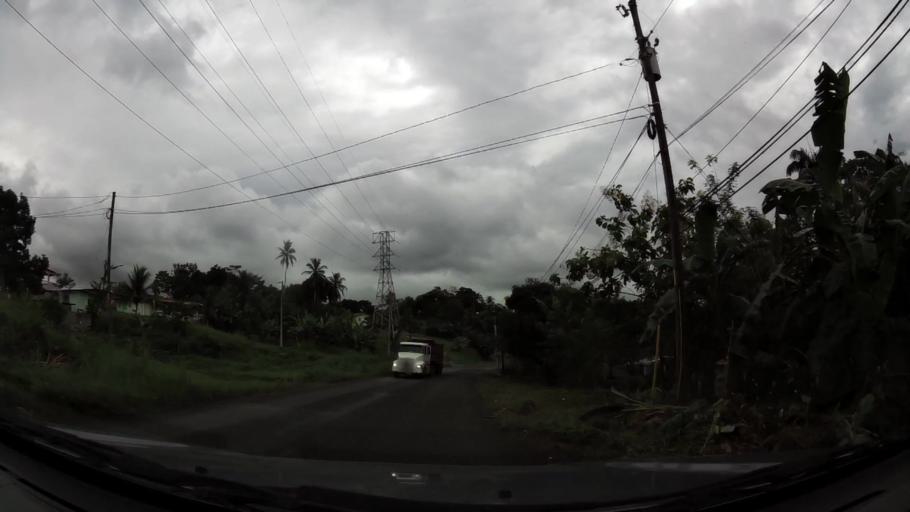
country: PA
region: Panama
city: Chilibre
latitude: 9.1780
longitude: -79.6114
